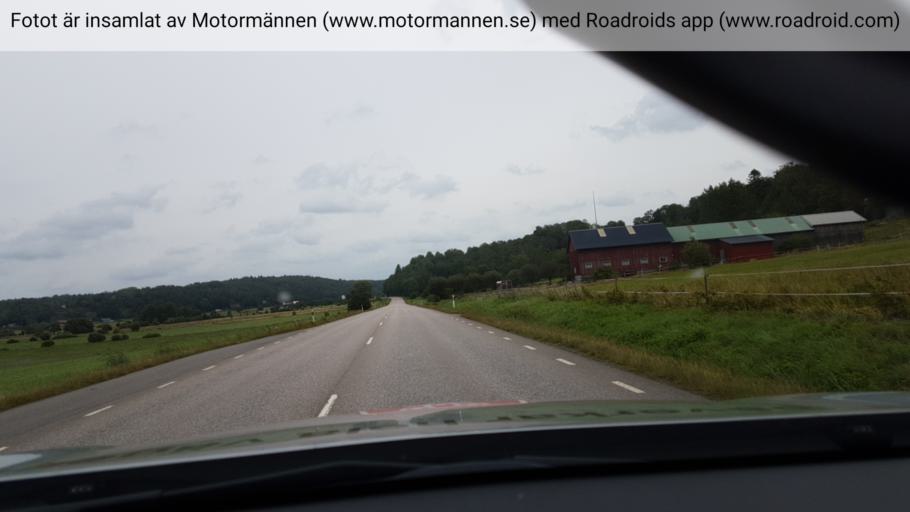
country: SE
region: Vaestra Goetaland
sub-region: Molndal
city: Lindome
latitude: 57.5945
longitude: 12.1439
